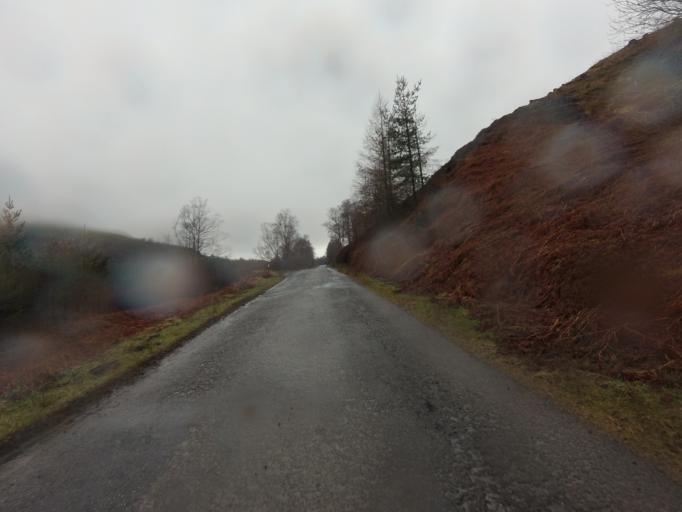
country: GB
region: Scotland
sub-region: West Dunbartonshire
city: Balloch
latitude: 56.2371
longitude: -4.5633
